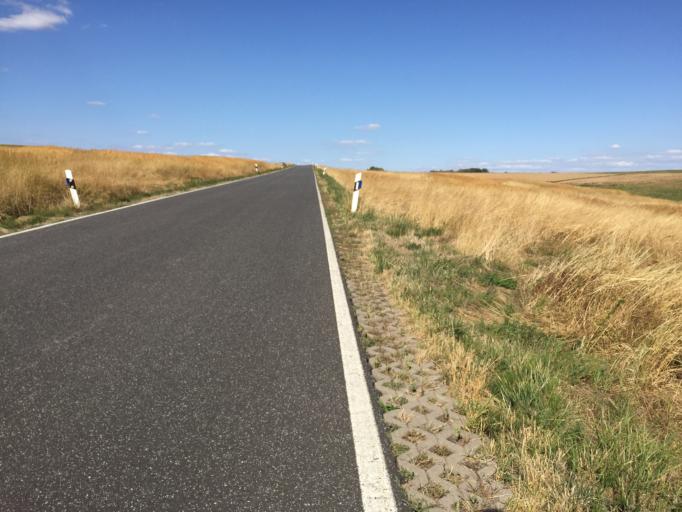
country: DE
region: Hesse
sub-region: Regierungsbezirk Giessen
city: Grunberg
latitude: 50.6064
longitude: 8.9286
